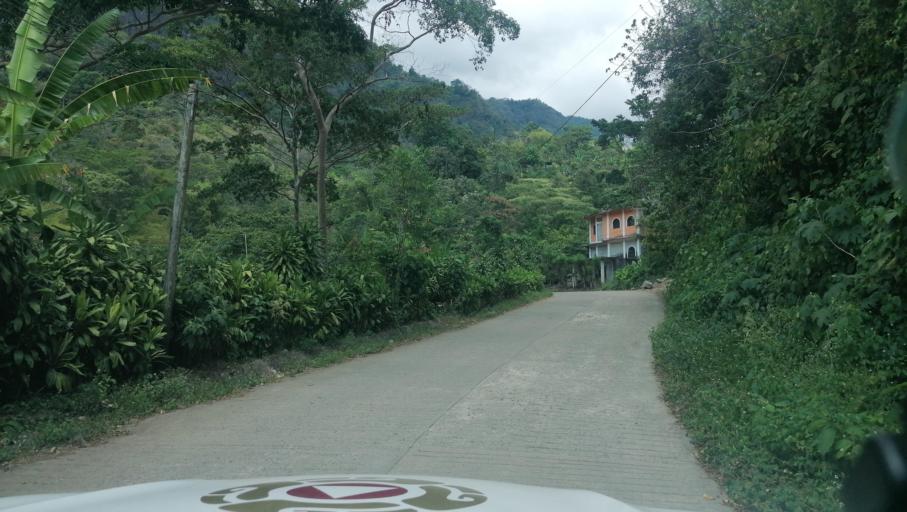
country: MX
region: Chiapas
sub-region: Cacahoatan
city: Benito Juarez
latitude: 15.1095
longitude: -92.2092
